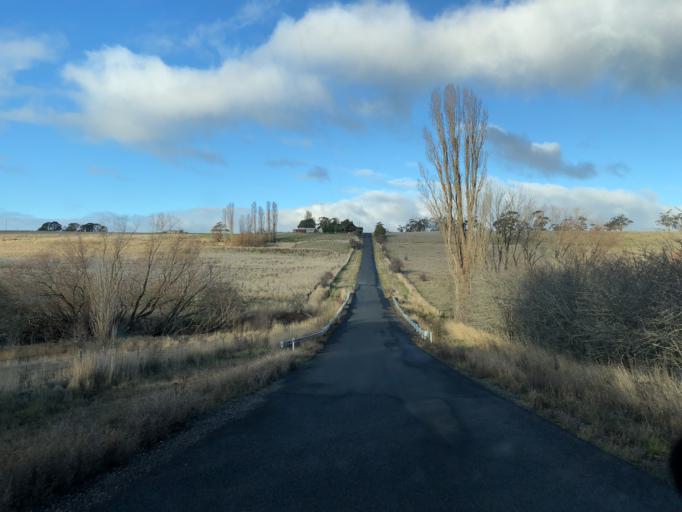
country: AU
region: Victoria
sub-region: Mount Alexander
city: Castlemaine
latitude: -37.2127
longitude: 144.3287
